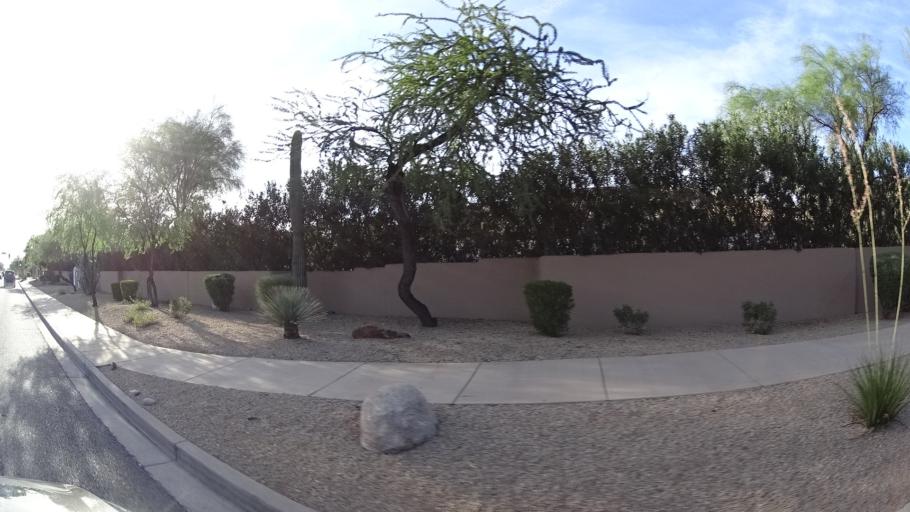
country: US
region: Arizona
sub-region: Maricopa County
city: Paradise Valley
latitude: 33.5310
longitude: -111.9444
